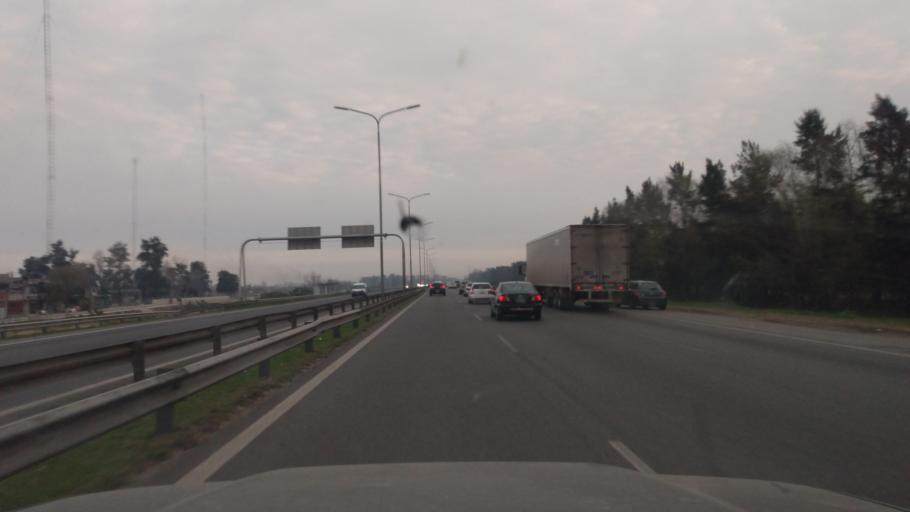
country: AR
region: Buenos Aires
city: Hurlingham
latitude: -34.5379
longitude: -58.5990
